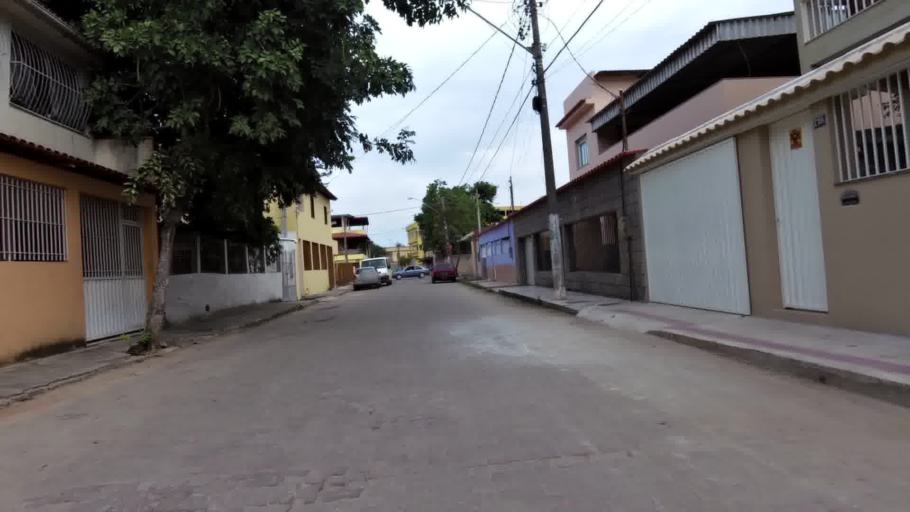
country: BR
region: Espirito Santo
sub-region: Piuma
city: Piuma
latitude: -20.8399
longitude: -40.7286
